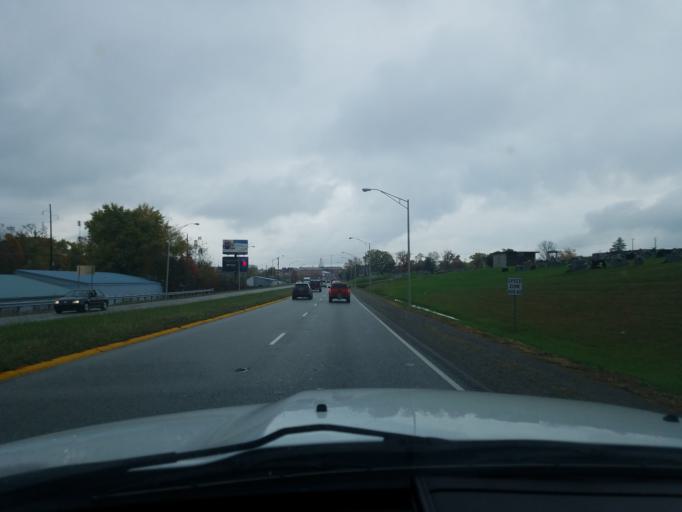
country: US
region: Kentucky
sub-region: Taylor County
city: Campbellsville
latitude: 37.3396
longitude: -85.3534
